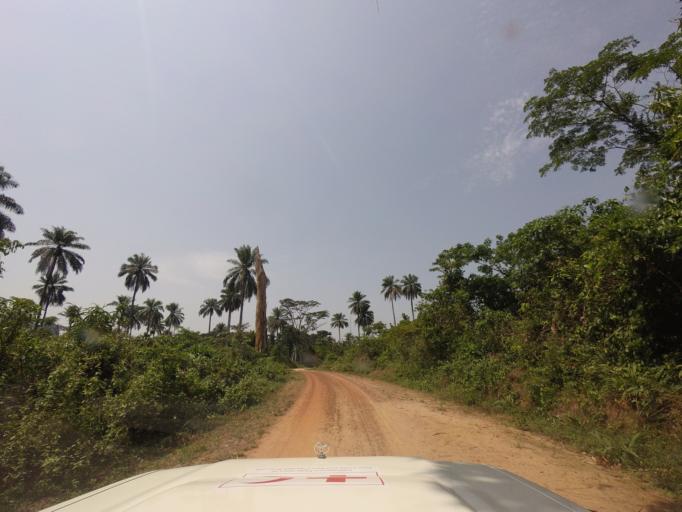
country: LR
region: Lofa
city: Voinjama
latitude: 8.4715
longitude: -9.6646
